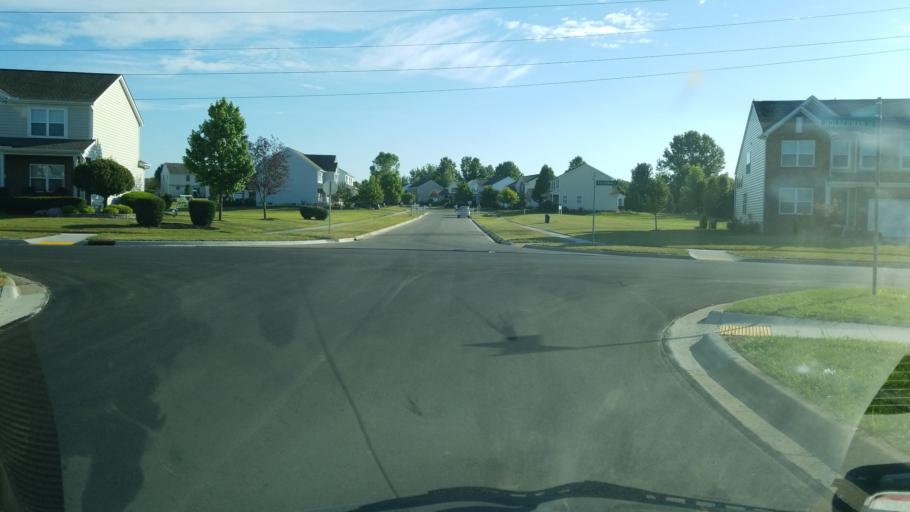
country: US
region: Ohio
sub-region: Delaware County
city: Lewis Center
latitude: 40.1755
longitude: -83.0012
